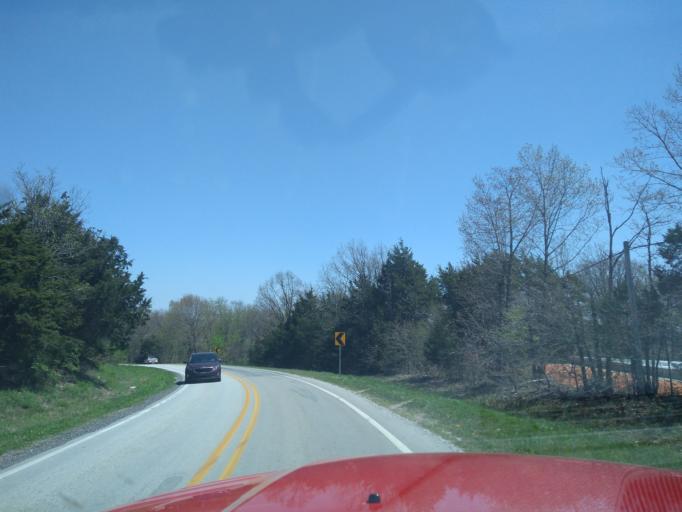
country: US
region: Arkansas
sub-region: Washington County
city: West Fork
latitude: 35.9011
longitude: -94.2056
